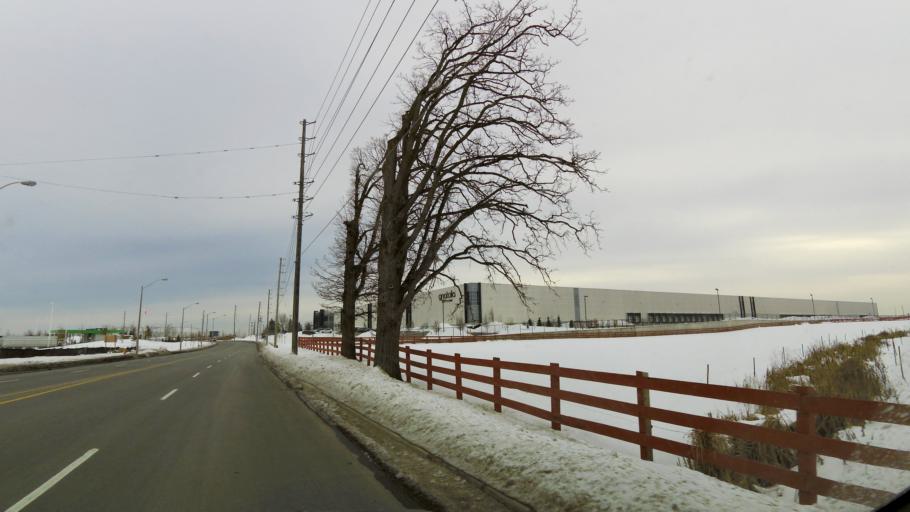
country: CA
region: Ontario
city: Brampton
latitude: 43.7835
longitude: -79.6504
